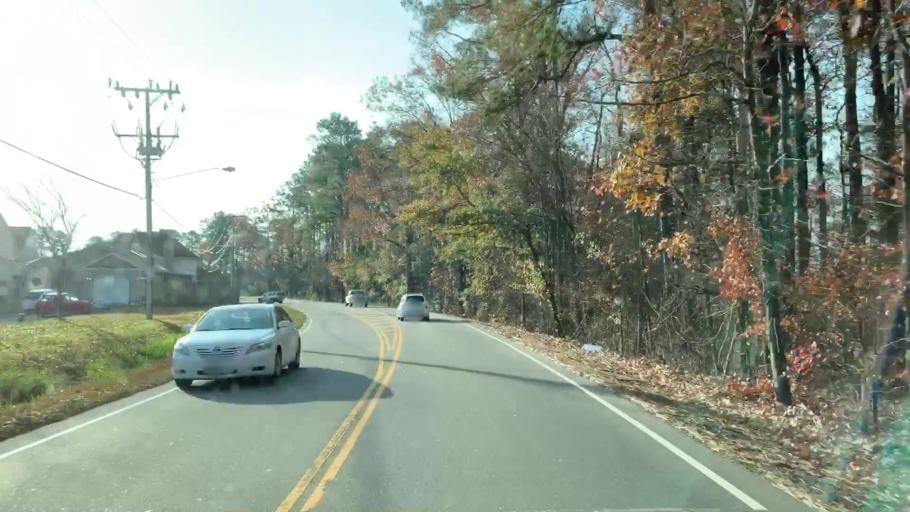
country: US
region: Virginia
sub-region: City of Chesapeake
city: Chesapeake
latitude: 36.7643
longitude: -76.1491
